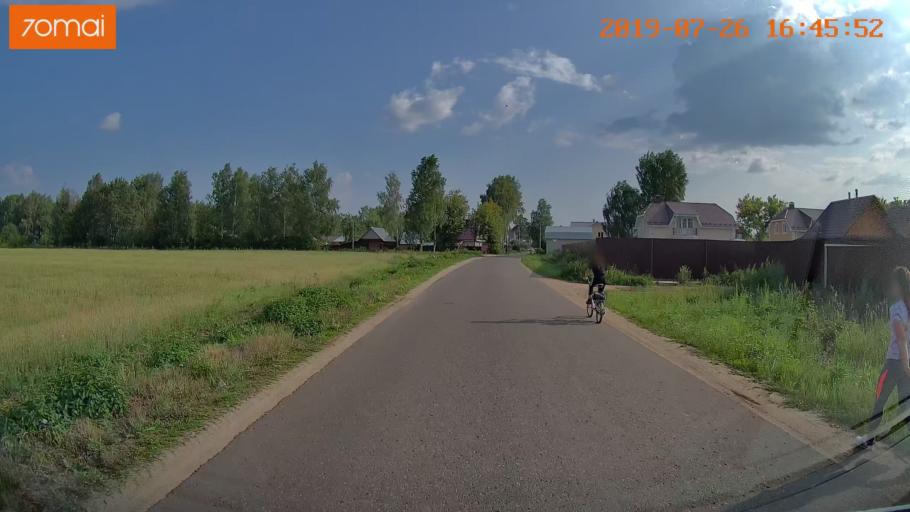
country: RU
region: Ivanovo
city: Bogorodskoye
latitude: 57.0454
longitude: 41.0221
